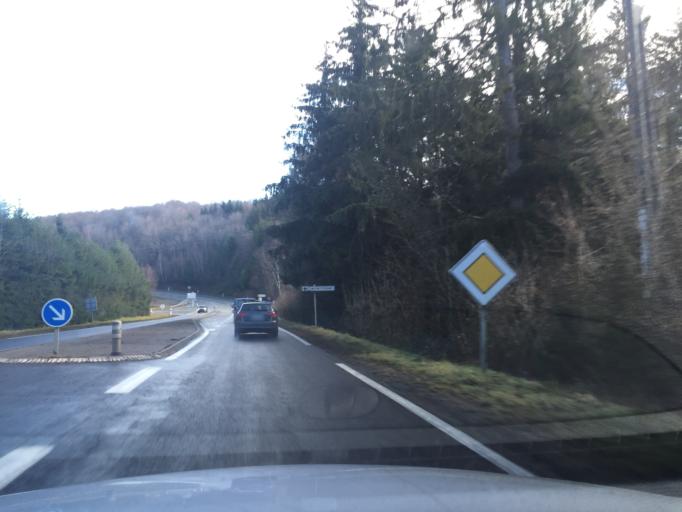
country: FR
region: Auvergne
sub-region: Departement du Puy-de-Dome
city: Saint-Ours
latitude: 45.8369
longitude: 2.8493
